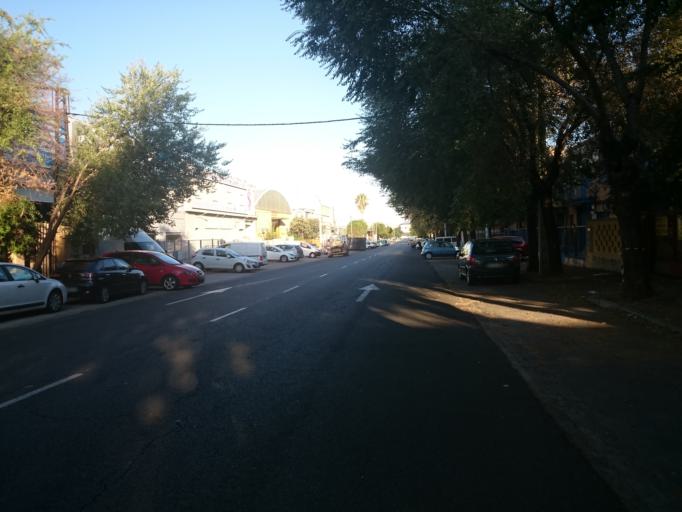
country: ES
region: Andalusia
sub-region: Provincia de Sevilla
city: Sevilla
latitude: 37.3884
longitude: -5.9519
